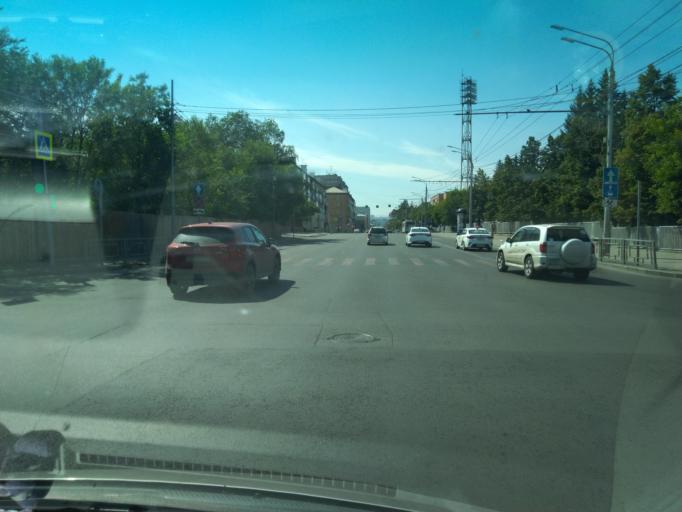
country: RU
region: Krasnoyarskiy
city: Krasnoyarsk
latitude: 56.0133
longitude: 92.8667
